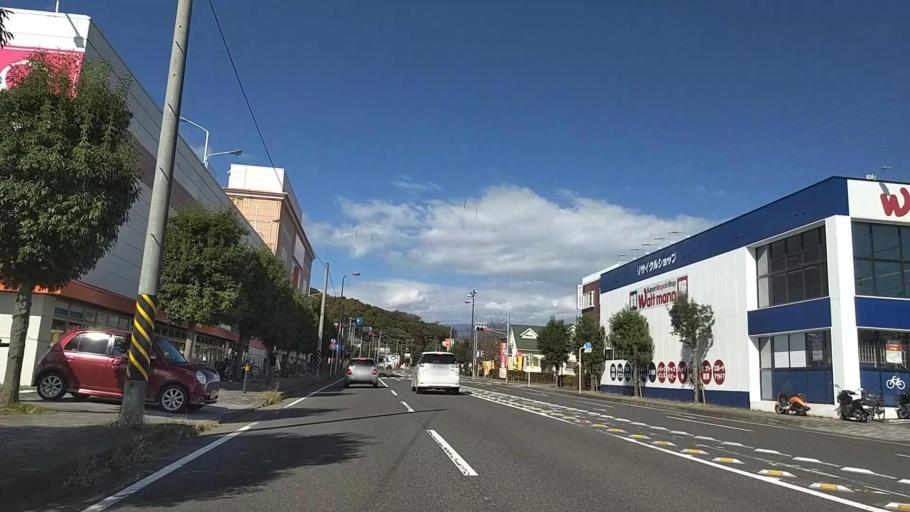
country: JP
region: Kanagawa
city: Ninomiya
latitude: 35.3144
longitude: 139.2436
